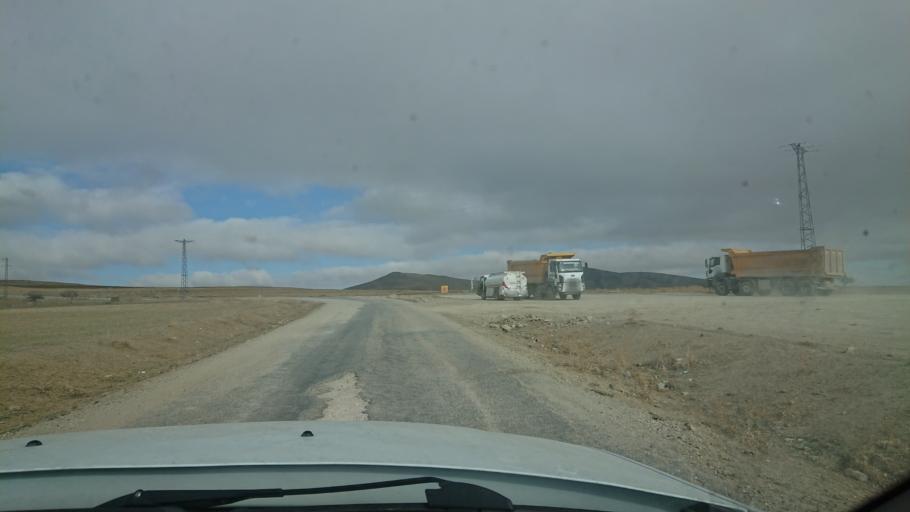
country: TR
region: Aksaray
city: Ortakoy
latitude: 38.7697
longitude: 34.0162
